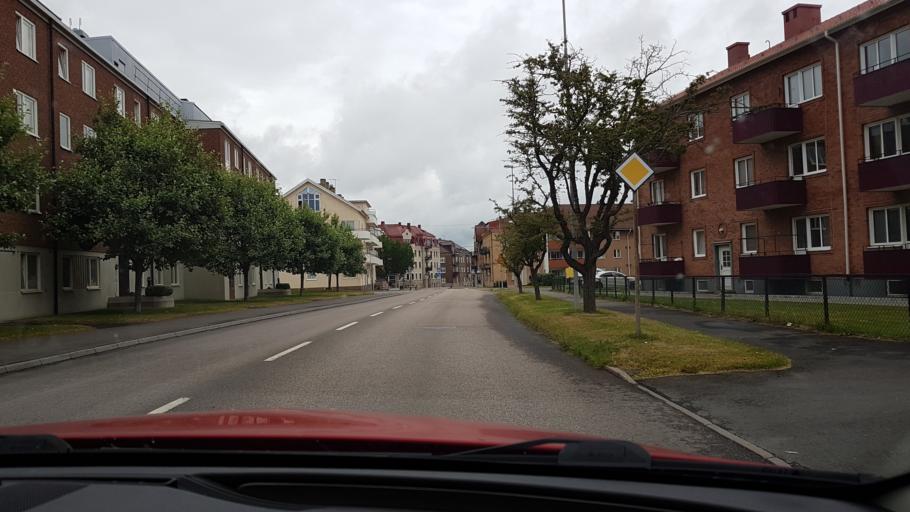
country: SE
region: Vaestra Goetaland
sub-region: Skovde Kommun
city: Skoevde
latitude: 58.3821
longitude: 13.8430
